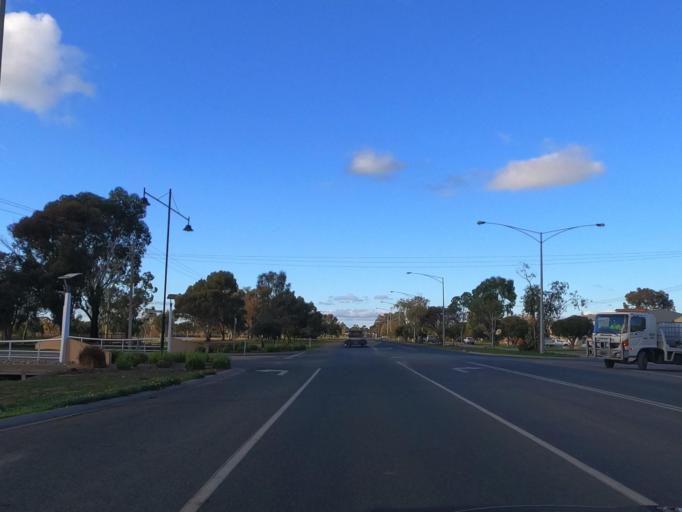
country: AU
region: Victoria
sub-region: Swan Hill
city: Swan Hill
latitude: -35.3417
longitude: 143.5351
